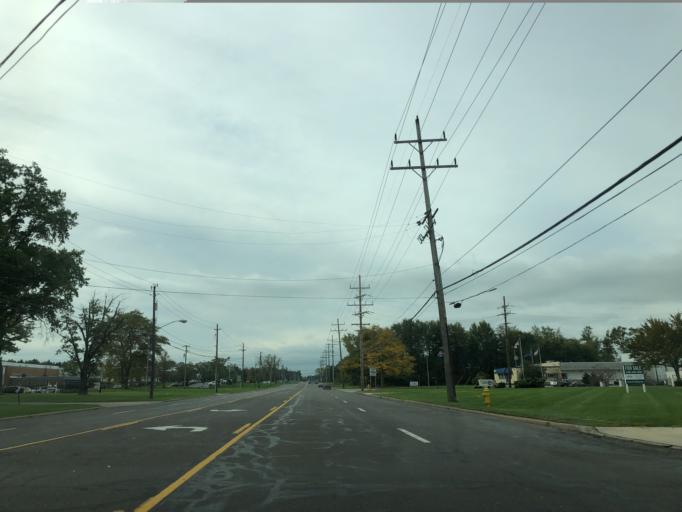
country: US
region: Ohio
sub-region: Cuyahoga County
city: Brecksville
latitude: 41.2876
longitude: -81.6272
